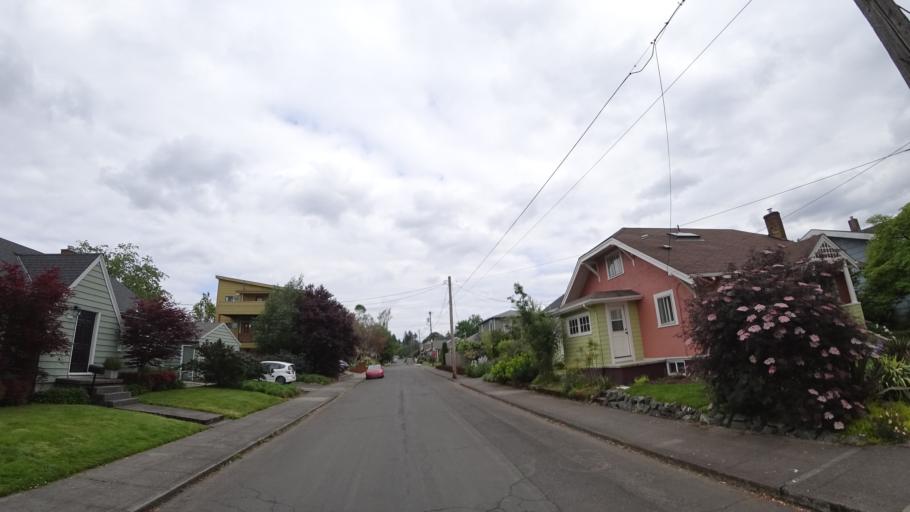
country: US
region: Oregon
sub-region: Multnomah County
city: Lents
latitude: 45.5067
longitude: -122.6161
